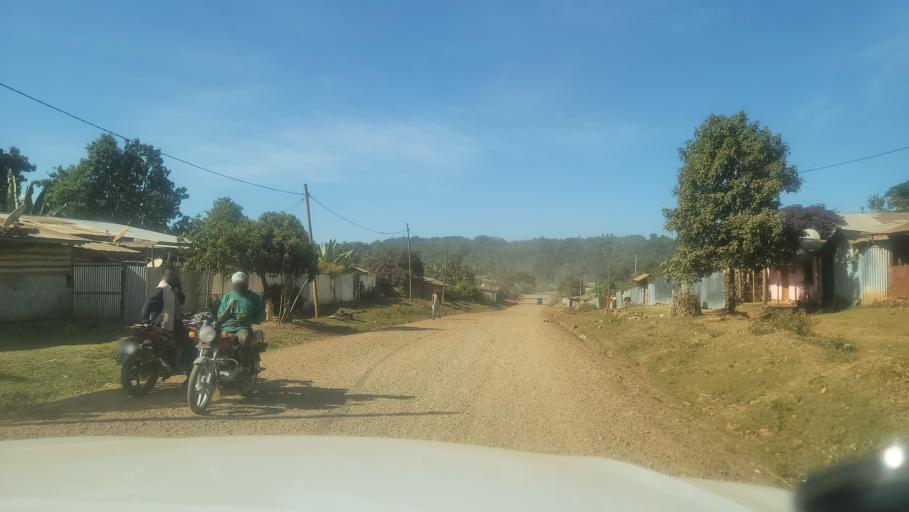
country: ET
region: Oromiya
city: Agaro
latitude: 7.8163
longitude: 36.5176
